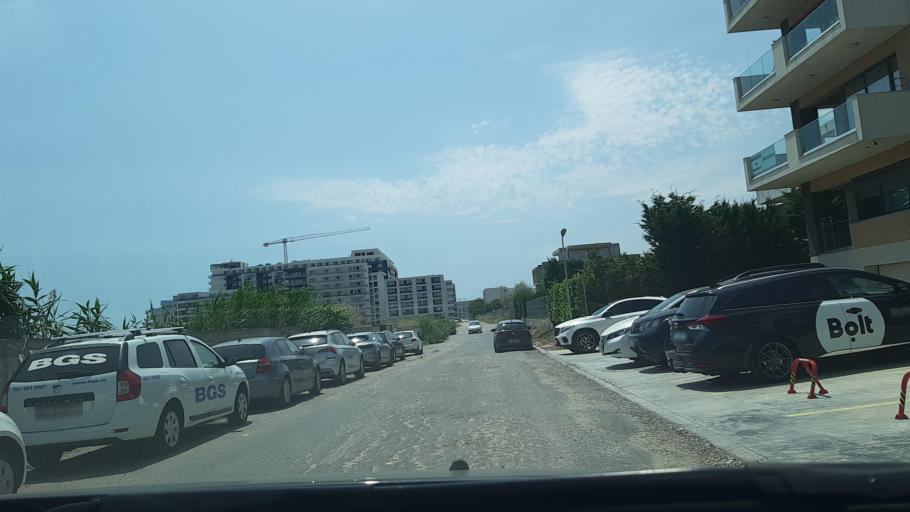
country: RO
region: Constanta
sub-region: Comuna Navodari
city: Navodari
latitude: 44.2979
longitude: 28.6234
